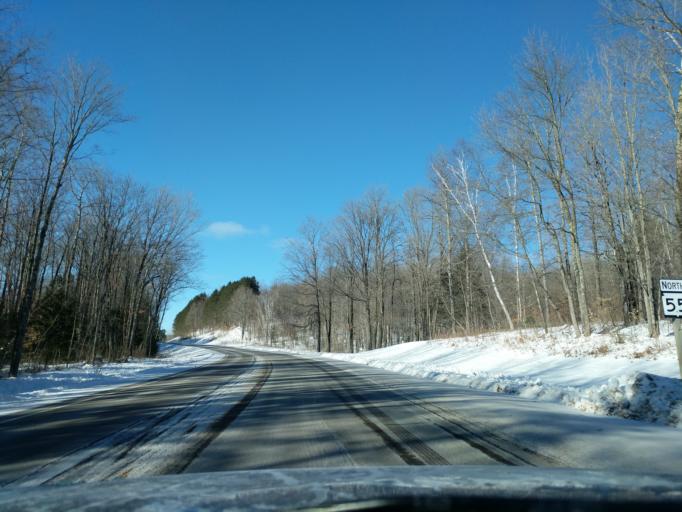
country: US
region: Wisconsin
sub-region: Menominee County
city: Keshena
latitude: 45.1281
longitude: -88.6635
